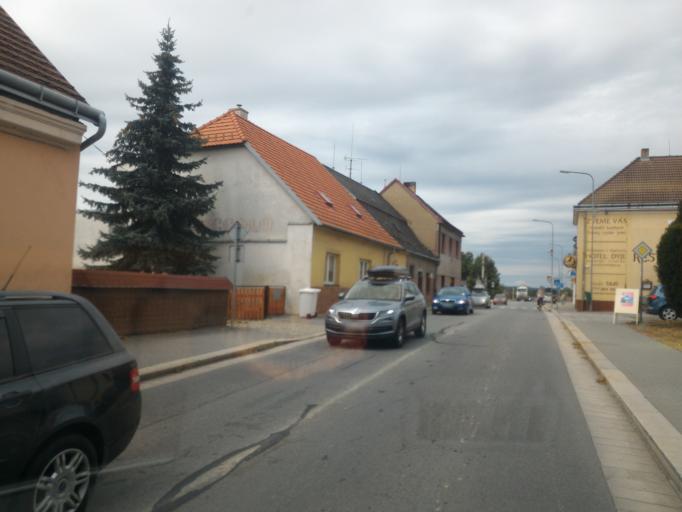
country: CZ
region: Jihocesky
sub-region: Okres Jindrichuv Hradec
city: Dacice
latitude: 49.0798
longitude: 15.4341
